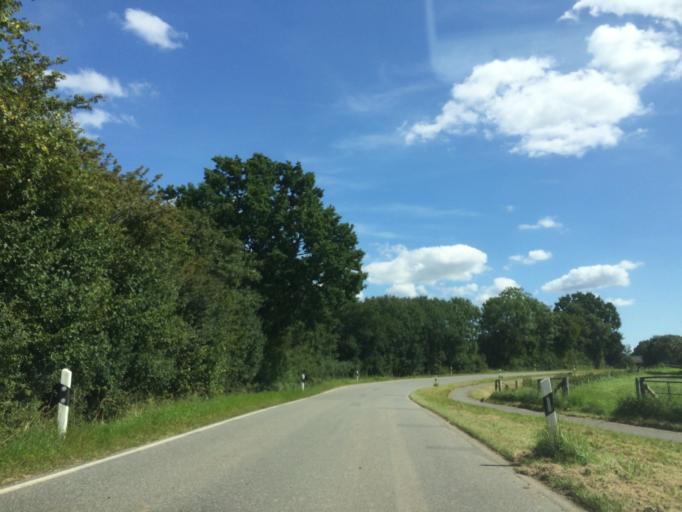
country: DE
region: Schleswig-Holstein
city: Grebin
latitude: 54.1966
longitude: 10.5078
